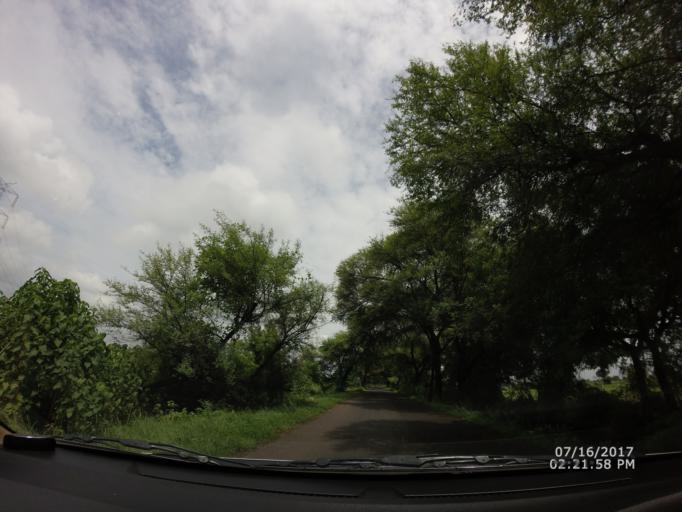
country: IN
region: Gujarat
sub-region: Mahesana
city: Kadi
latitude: 23.1367
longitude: 72.2905
